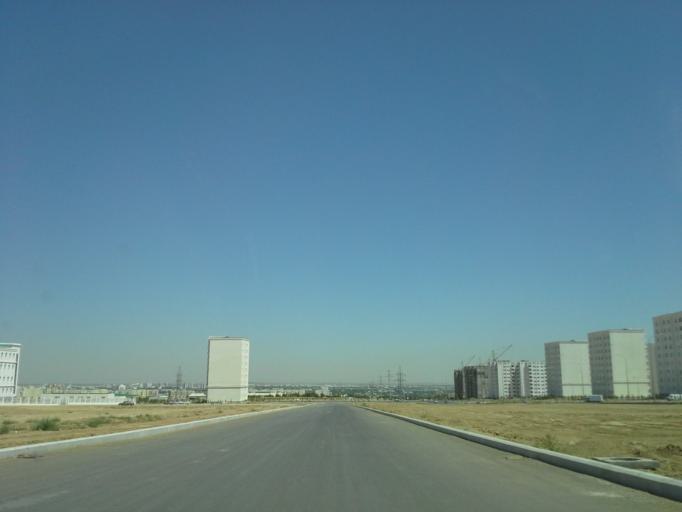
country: TM
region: Ahal
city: Ashgabat
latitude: 37.8908
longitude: 58.4047
